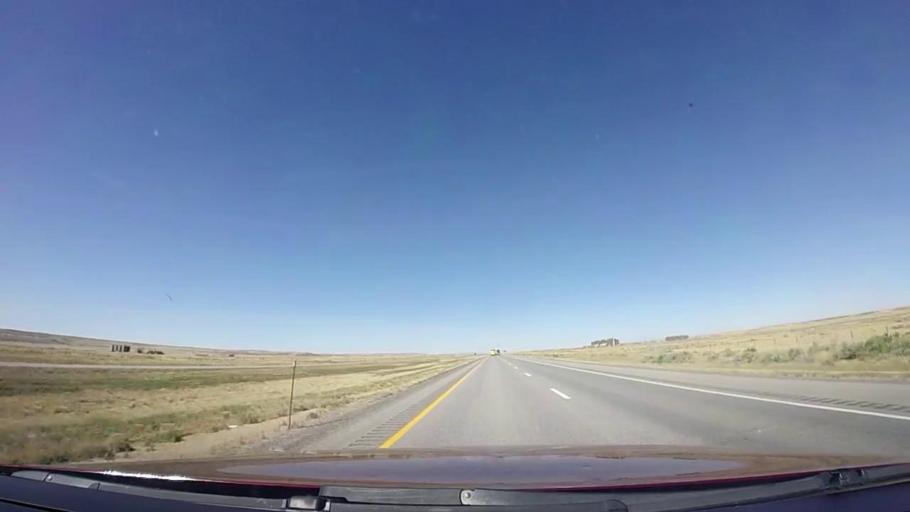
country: US
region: Wyoming
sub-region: Carbon County
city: Rawlins
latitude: 41.6678
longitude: -108.0155
